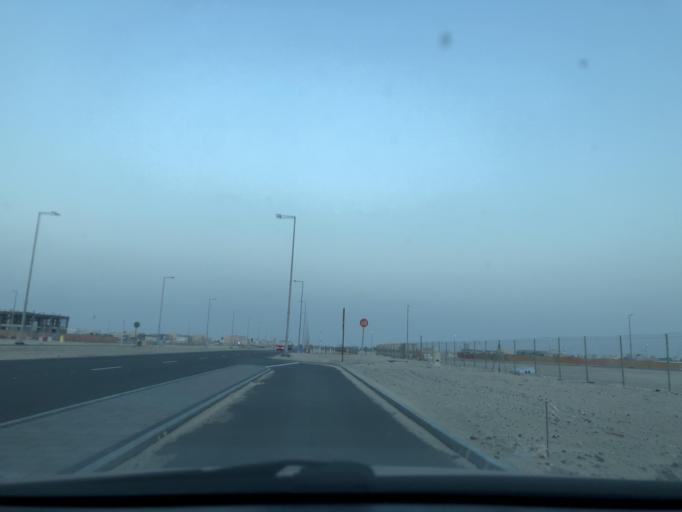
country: AE
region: Abu Dhabi
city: Abu Dhabi
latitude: 24.3602
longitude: 54.6070
